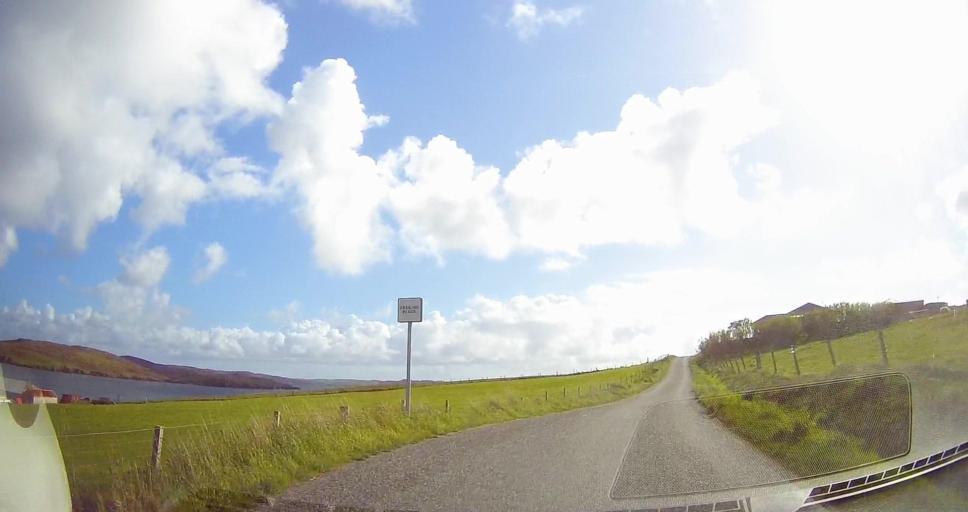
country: GB
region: Scotland
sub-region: Shetland Islands
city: Lerwick
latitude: 60.3544
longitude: -1.3917
